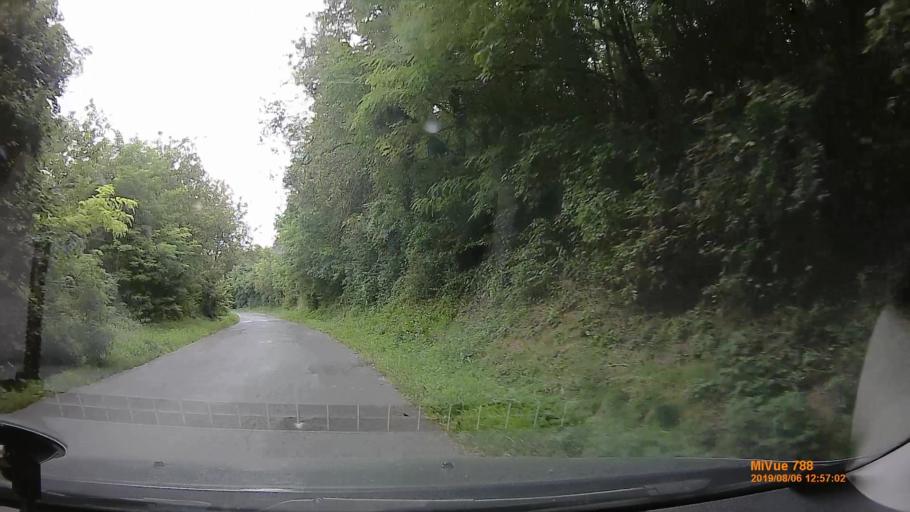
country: HU
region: Zala
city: Pacsa
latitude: 46.6341
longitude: 17.0354
